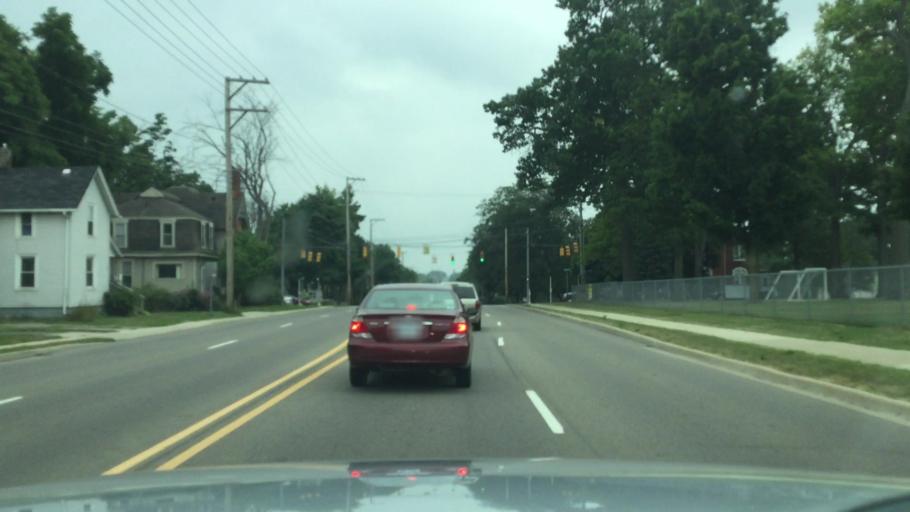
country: US
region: Michigan
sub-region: Shiawassee County
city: Owosso
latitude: 43.0028
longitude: -84.1769
